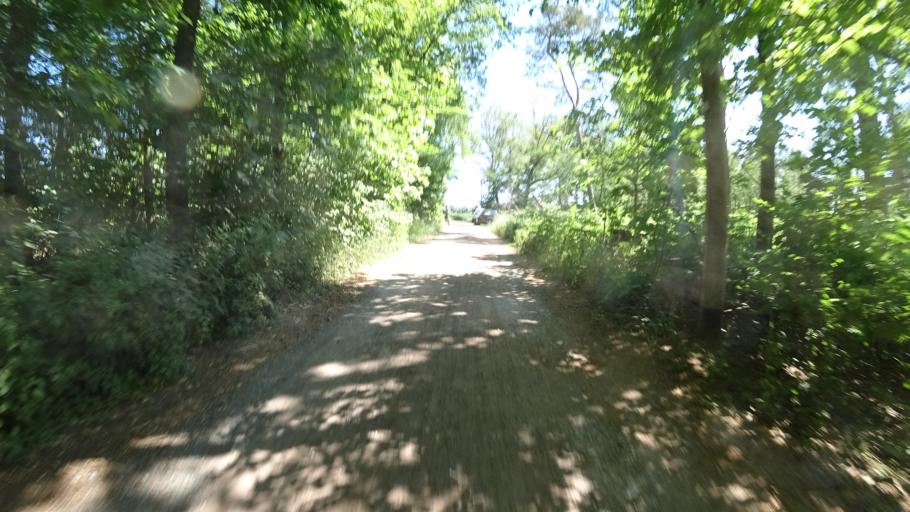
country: DE
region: North Rhine-Westphalia
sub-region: Regierungsbezirk Detmold
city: Rheda-Wiedenbruck
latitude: 51.8544
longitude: 8.3423
